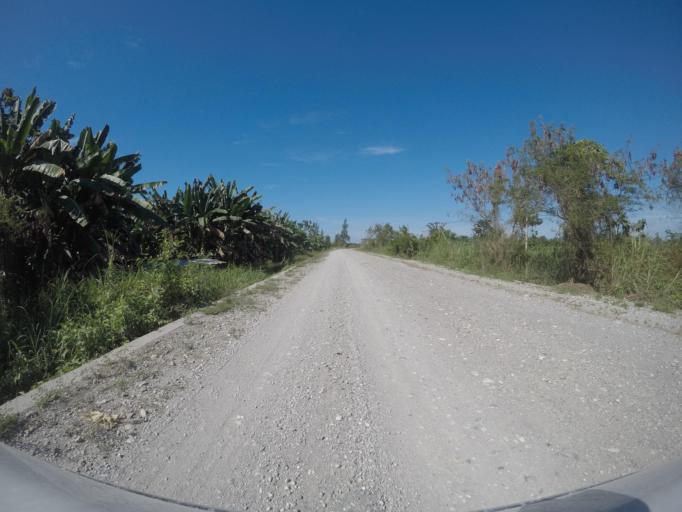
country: TL
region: Viqueque
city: Viqueque
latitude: -8.9444
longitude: 126.1124
